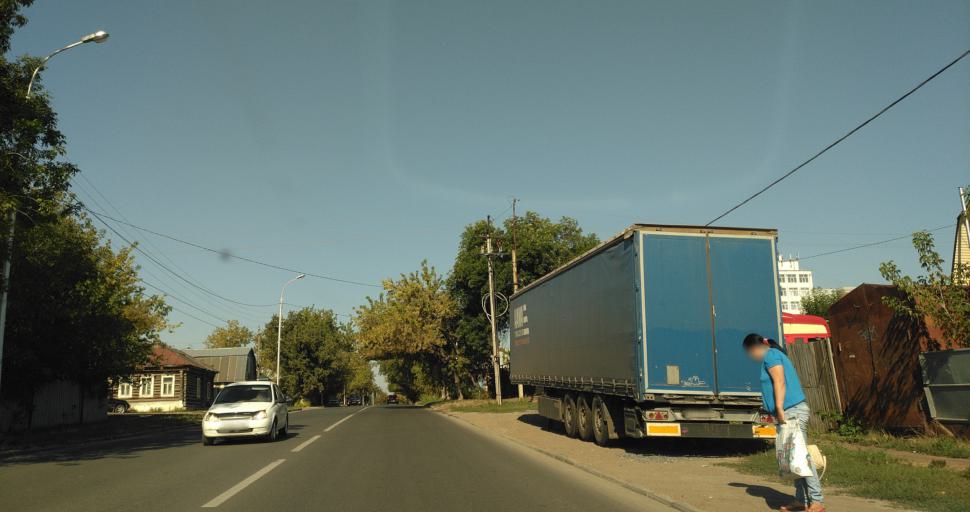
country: RU
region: Bashkortostan
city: Ufa
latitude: 54.7246
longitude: 55.9734
